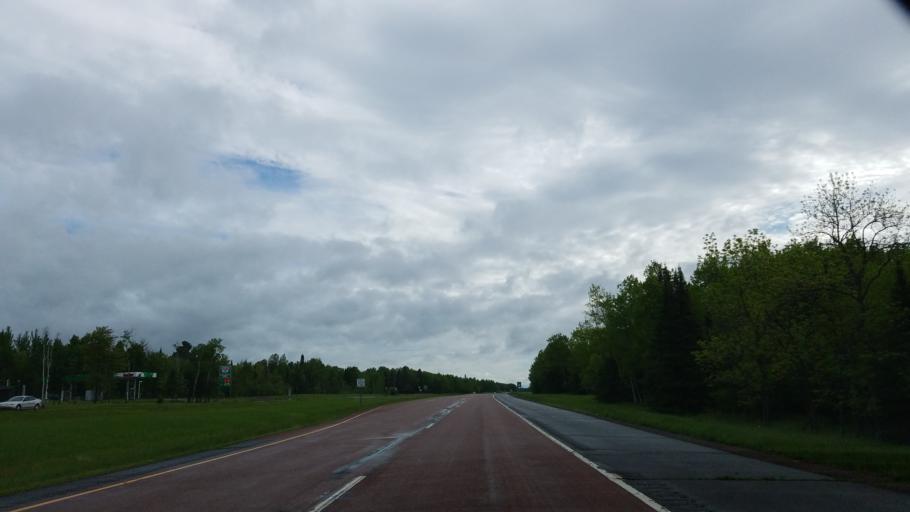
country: US
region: Minnesota
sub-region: Saint Louis County
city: Arnold
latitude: 46.8842
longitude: -91.9312
